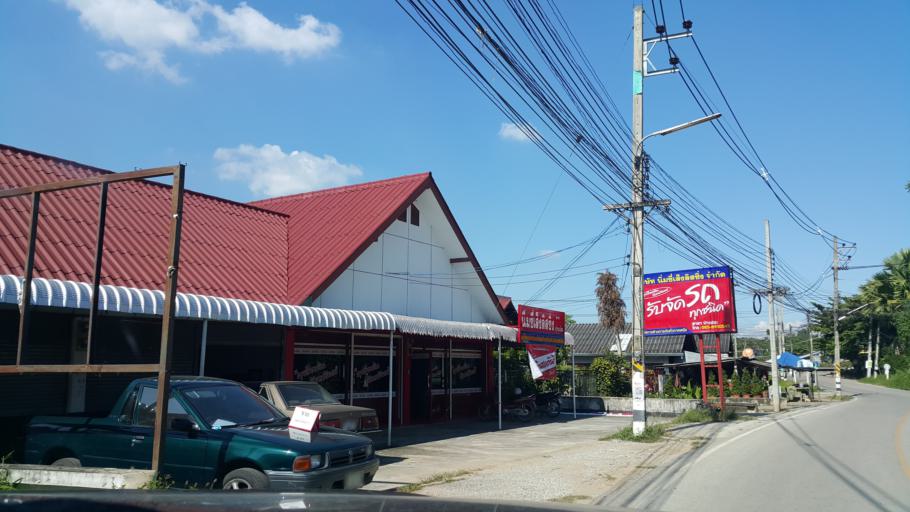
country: TH
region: Chiang Mai
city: Chiang Mai
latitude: 18.7435
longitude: 98.9902
